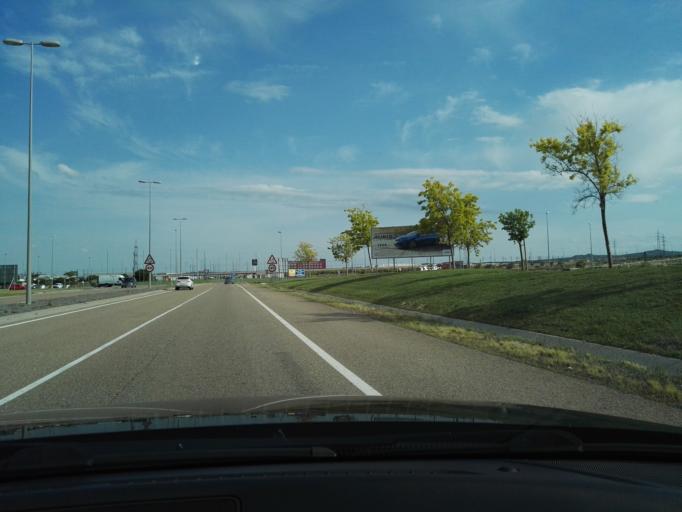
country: ES
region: Aragon
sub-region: Provincia de Zaragoza
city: Montecanal
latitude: 41.6411
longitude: -0.9932
